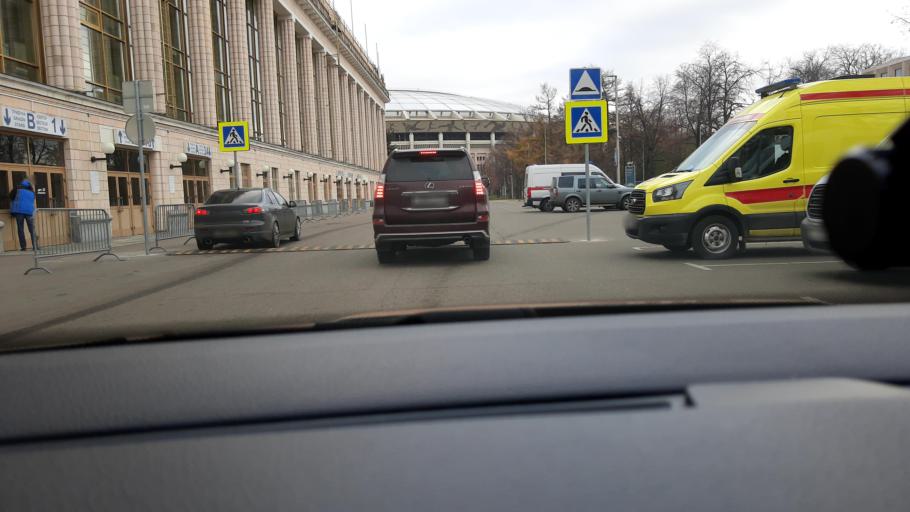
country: RU
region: Moscow
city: Luzhniki
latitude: 55.7183
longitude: 37.5482
